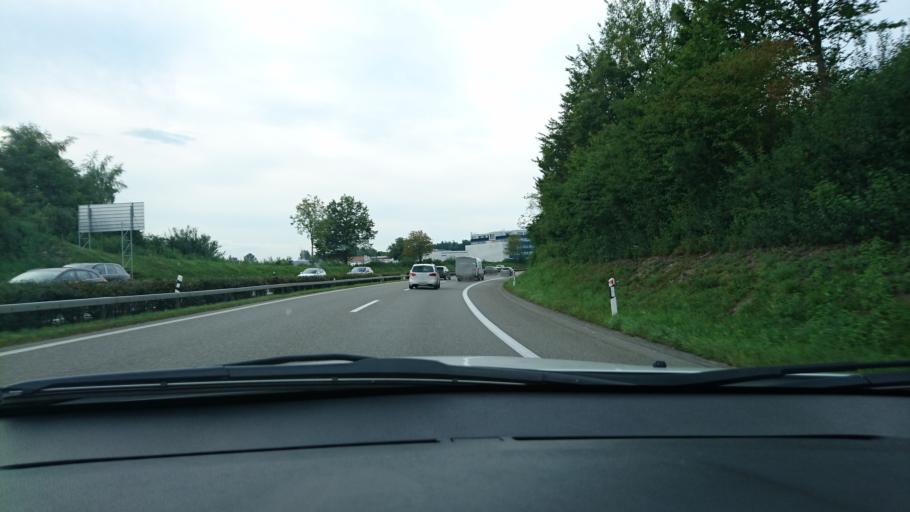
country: CH
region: Zurich
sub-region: Bezirk Uster
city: Hegnau
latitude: 47.3885
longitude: 8.6703
